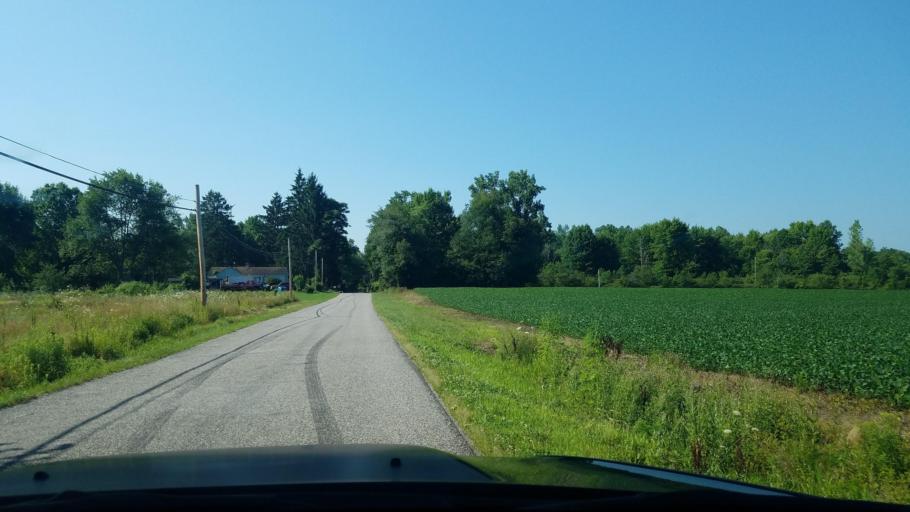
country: US
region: Ohio
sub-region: Trumbull County
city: Leavittsburg
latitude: 41.2625
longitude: -80.9249
